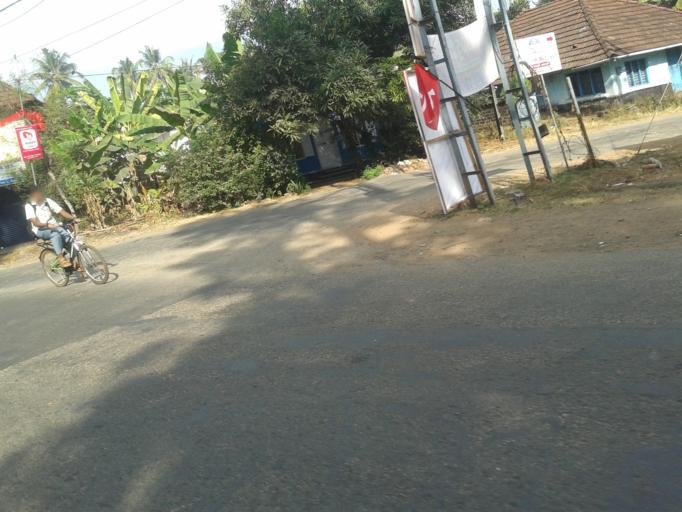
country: IN
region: Kerala
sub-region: Thrissur District
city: Kizhake Chalakudi
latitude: 10.3056
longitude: 76.3308
